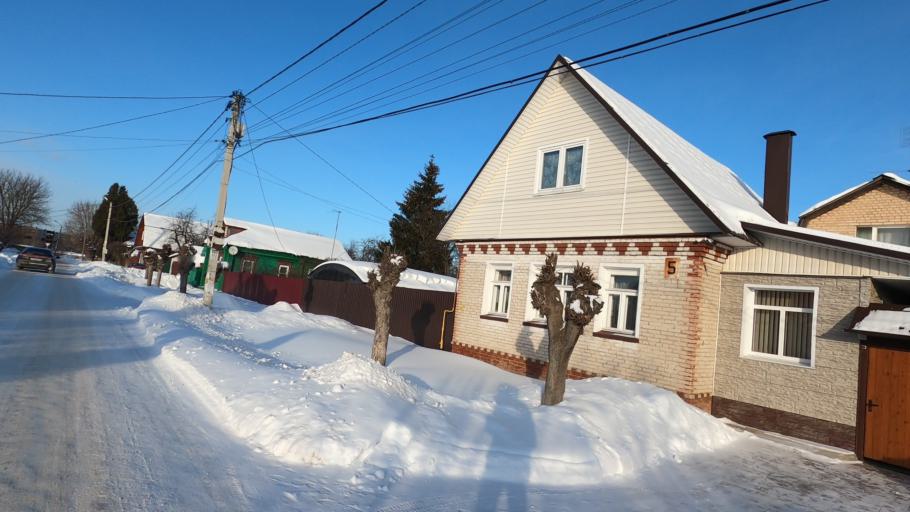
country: RU
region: Moskovskaya
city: Pavlovskiy Posad
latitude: 55.7714
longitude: 38.6977
